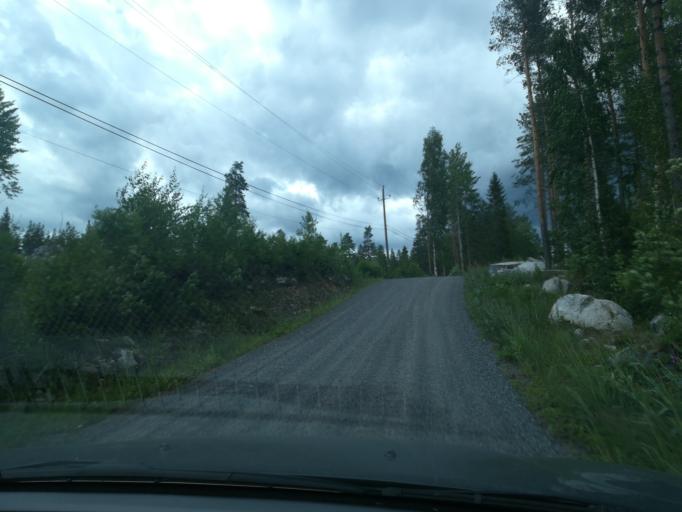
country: FI
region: Southern Savonia
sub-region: Mikkeli
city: Mikkeli
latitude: 61.6612
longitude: 27.1163
